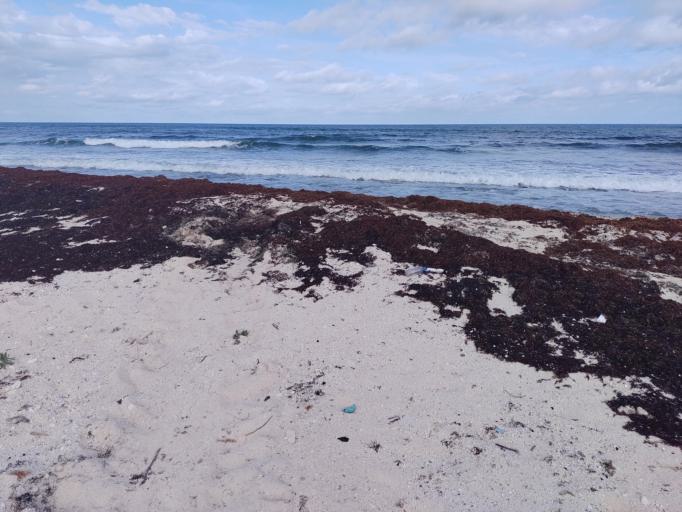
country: MX
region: Quintana Roo
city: San Miguel de Cozumel
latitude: 20.4247
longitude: -86.8419
